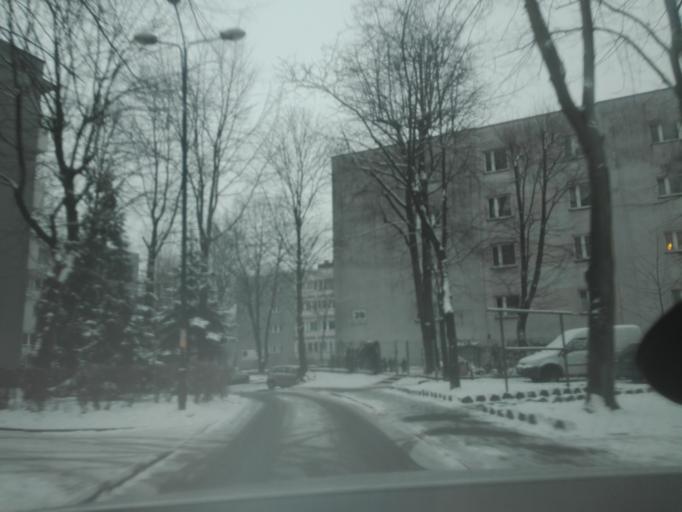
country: PL
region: Silesian Voivodeship
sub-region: Chorzow
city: Chorzow
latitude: 50.2766
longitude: 18.9768
